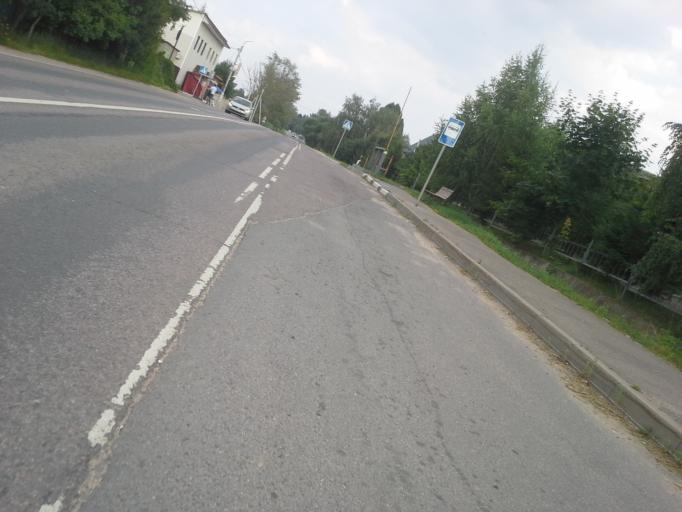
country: RU
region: Moskovskaya
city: Istra
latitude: 55.9314
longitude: 36.9306
